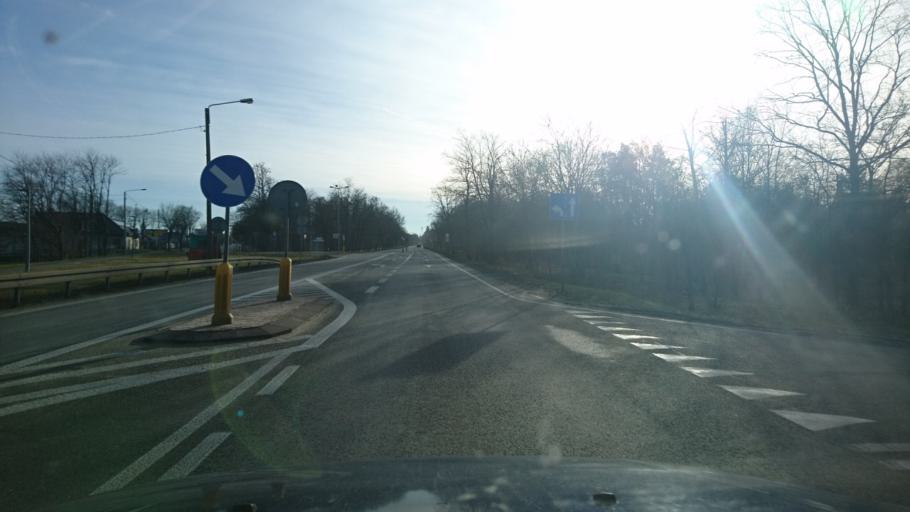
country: PL
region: Greater Poland Voivodeship
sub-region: Powiat ostrzeszowski
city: Ostrzeszow
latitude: 51.4347
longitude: 17.9160
